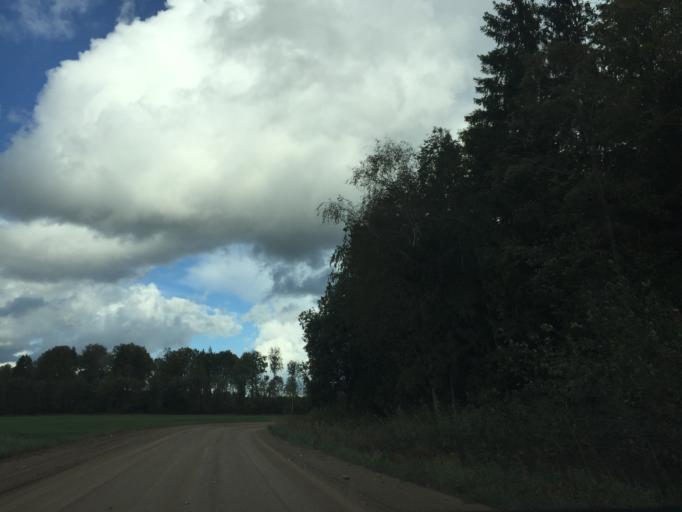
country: LV
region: Malpils
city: Malpils
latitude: 57.0563
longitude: 25.1310
